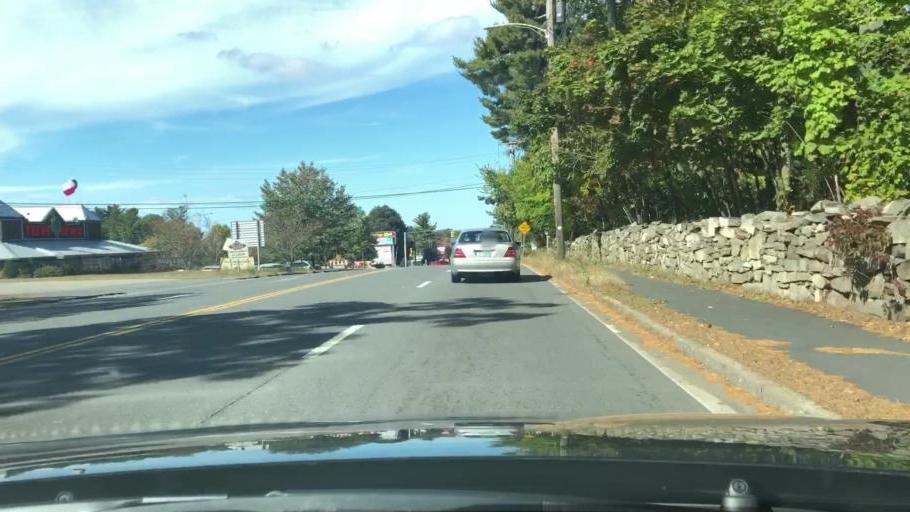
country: US
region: Massachusetts
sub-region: Essex County
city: Methuen
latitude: 42.7356
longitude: -71.1933
